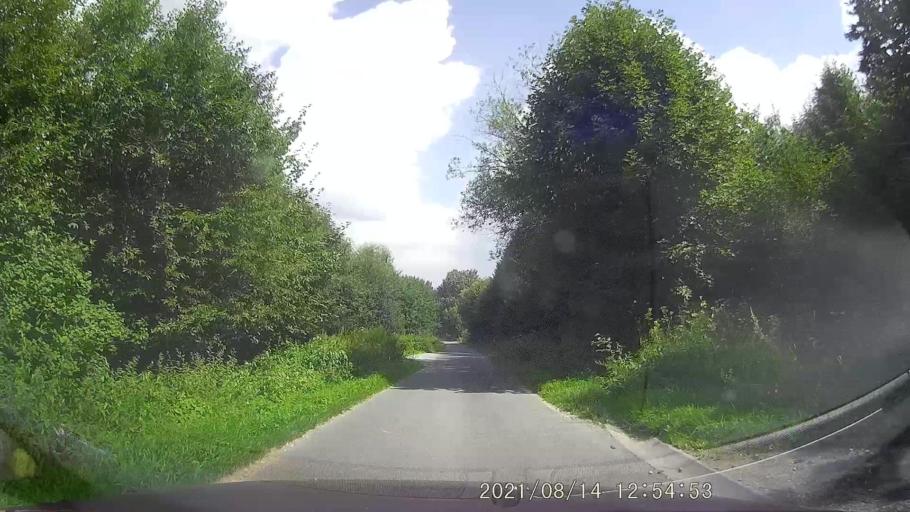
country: PL
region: Lower Silesian Voivodeship
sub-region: Powiat klodzki
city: Ladek-Zdroj
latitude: 50.3295
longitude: 16.8244
